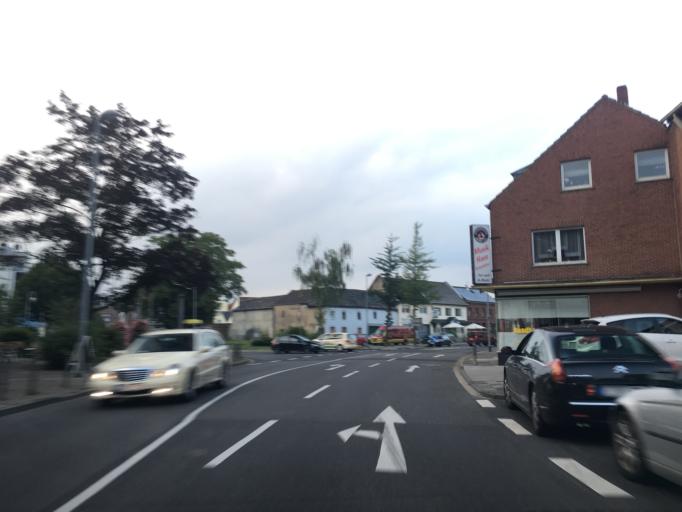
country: DE
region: North Rhine-Westphalia
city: Huckelhoven
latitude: 51.0523
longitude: 6.2266
